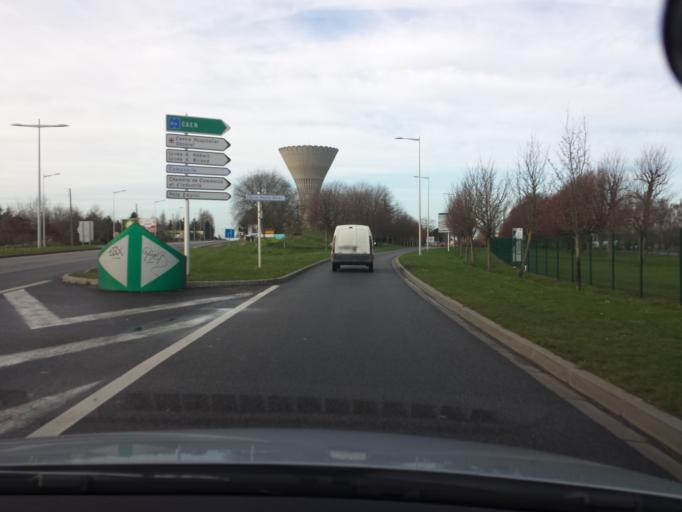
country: FR
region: Haute-Normandie
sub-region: Departement de l'Eure
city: Evreux
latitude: 49.0158
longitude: 1.1754
